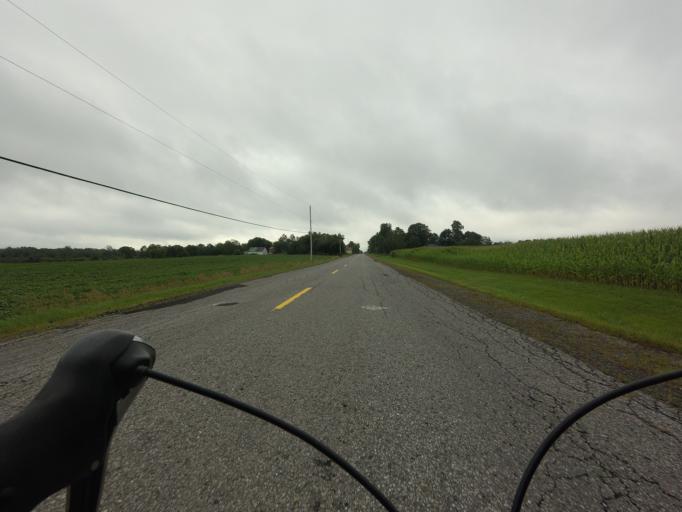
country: CA
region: Ontario
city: Bells Corners
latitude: 45.1099
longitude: -75.7792
